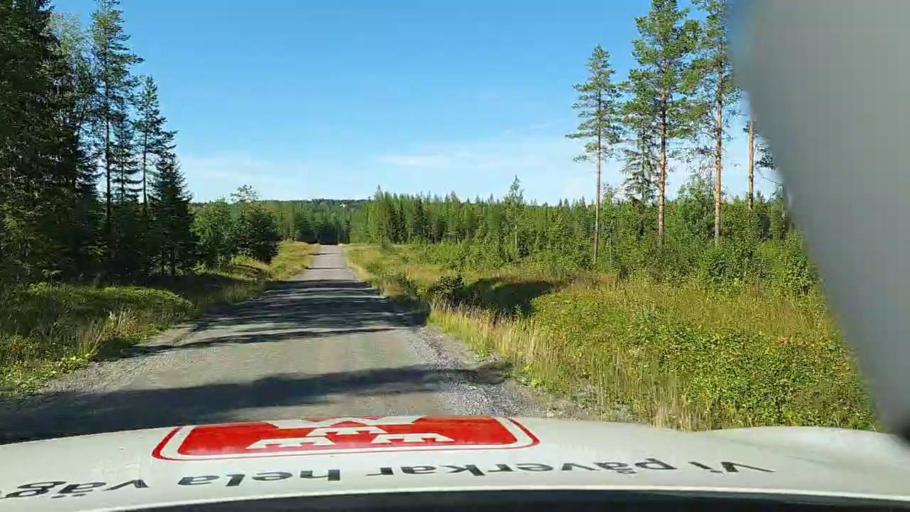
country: SE
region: Jaemtland
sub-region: OEstersunds Kommun
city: Lit
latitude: 63.7655
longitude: 14.6613
